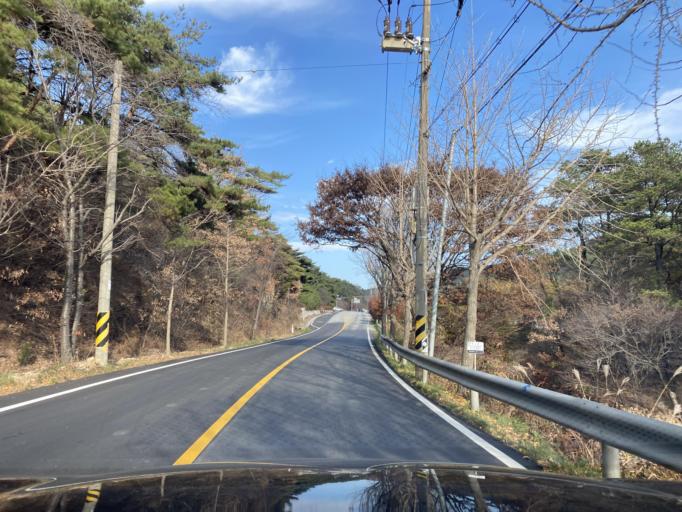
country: KR
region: Chungcheongnam-do
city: Hongsung
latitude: 36.6554
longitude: 126.6229
